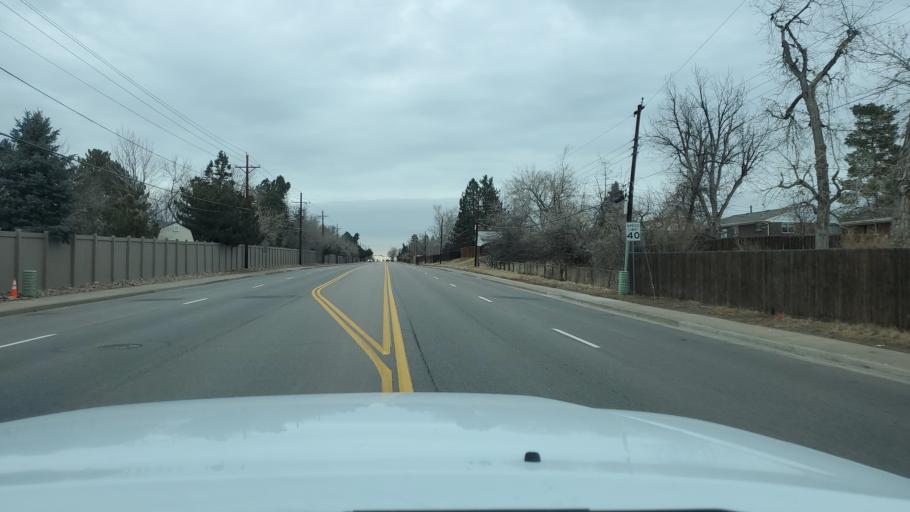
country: US
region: Colorado
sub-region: Arapahoe County
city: Southglenn
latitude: 39.5886
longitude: -104.9415
